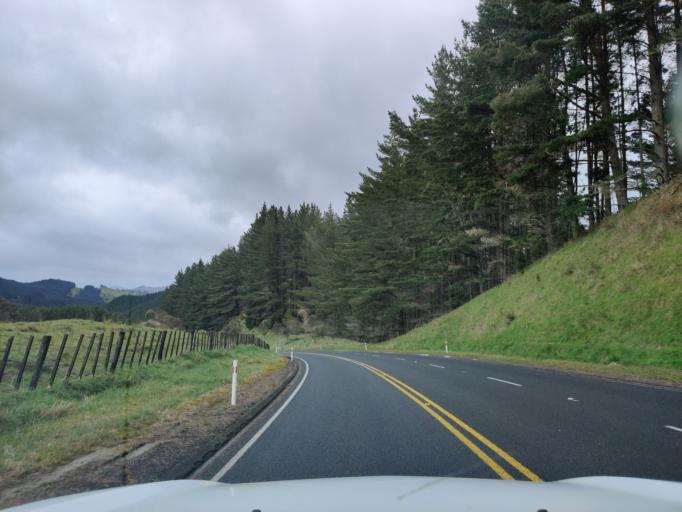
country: NZ
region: Waikato
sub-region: Otorohanga District
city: Otorohanga
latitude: -38.6407
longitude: 175.2057
